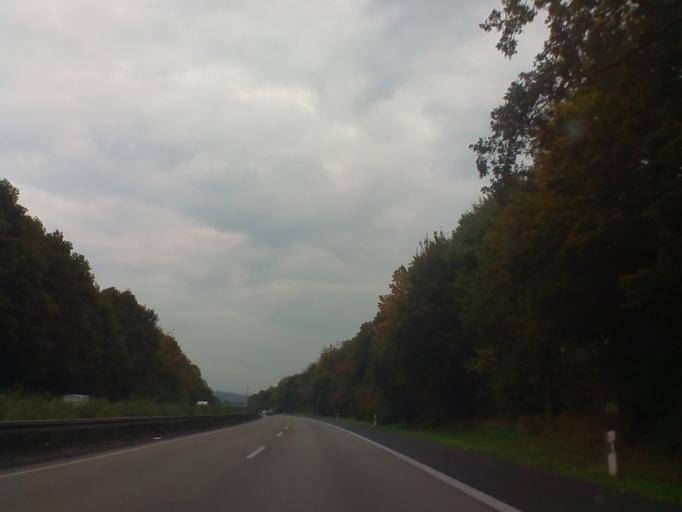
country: DE
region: Hesse
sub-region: Regierungsbezirk Kassel
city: Kunzell
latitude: 50.5348
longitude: 9.7315
